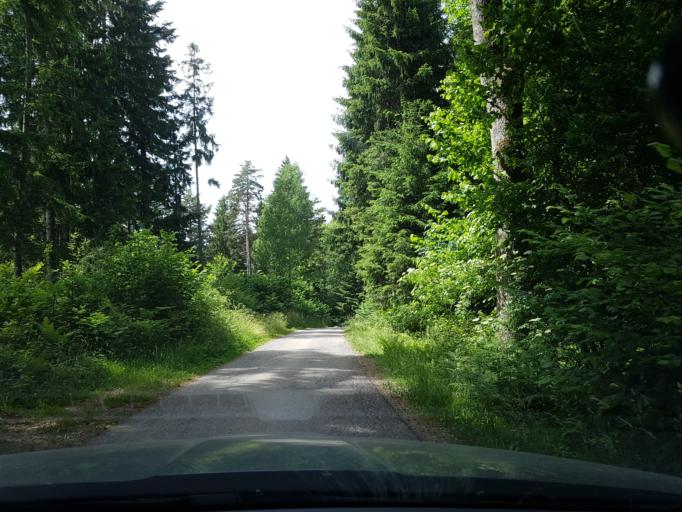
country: AT
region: Carinthia
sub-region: Politischer Bezirk Spittal an der Drau
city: Millstatt
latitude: 46.7802
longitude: 13.5540
